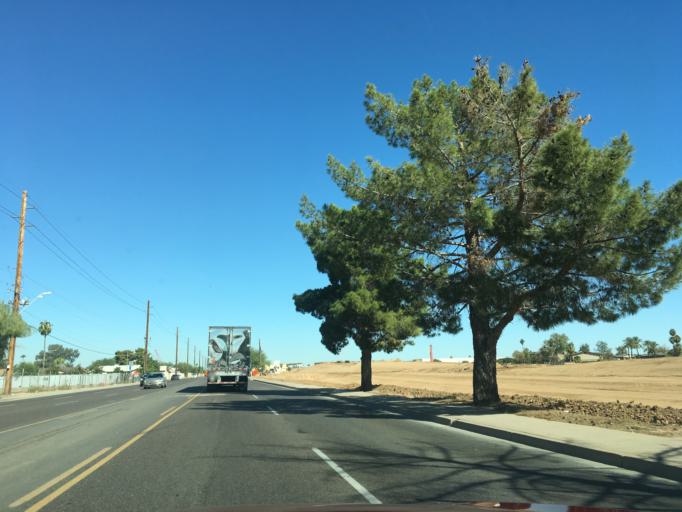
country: US
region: Arizona
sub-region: Maricopa County
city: Tolleson
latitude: 33.4534
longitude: -112.1865
